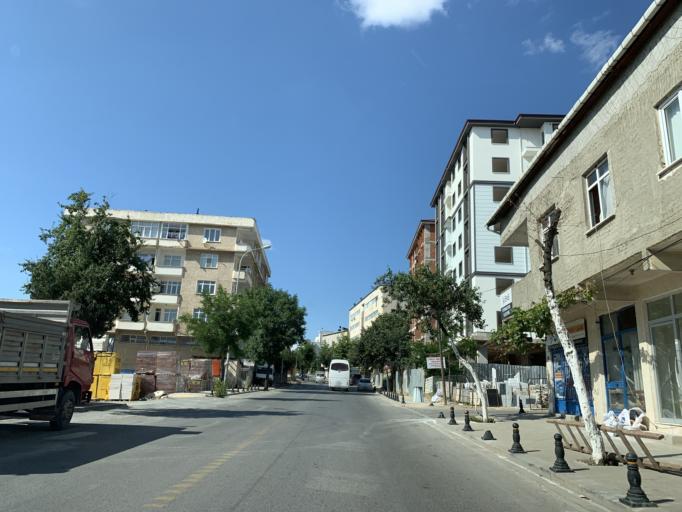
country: TR
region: Istanbul
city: Pendik
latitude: 40.8837
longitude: 29.2828
